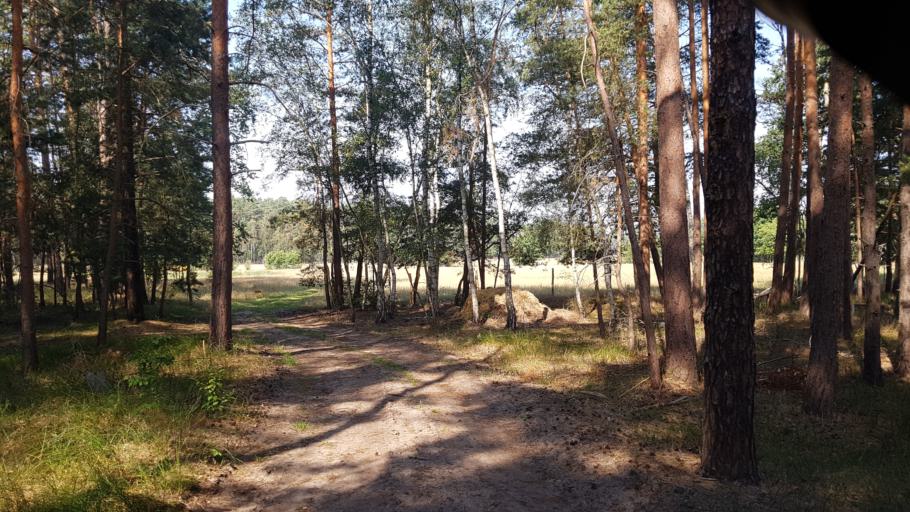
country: DE
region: Brandenburg
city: Cottbus
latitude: 51.7059
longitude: 14.4125
